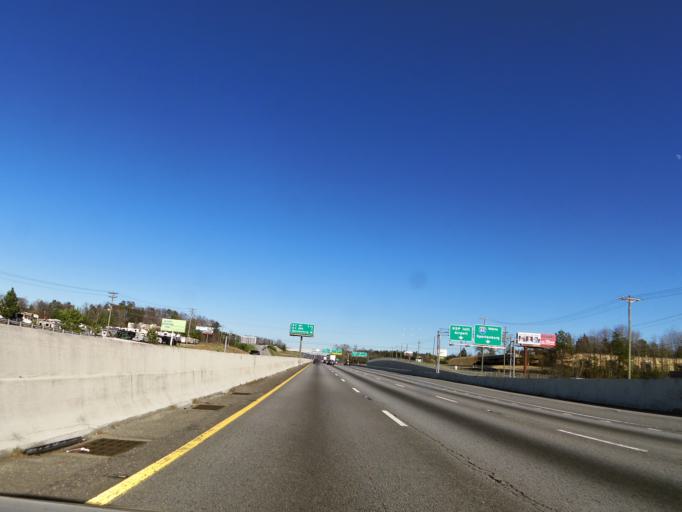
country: US
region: South Carolina
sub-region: Greenville County
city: Greer
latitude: 34.8732
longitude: -82.2220
